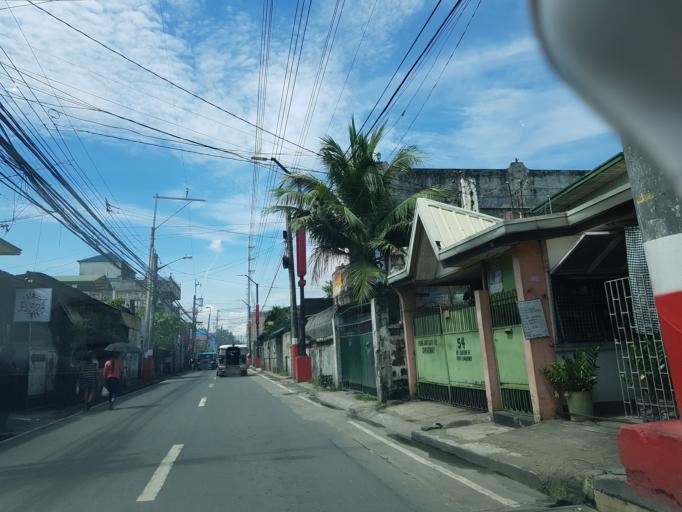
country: PH
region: Calabarzon
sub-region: Province of Rizal
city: Taguig
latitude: 14.5165
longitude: 121.0721
